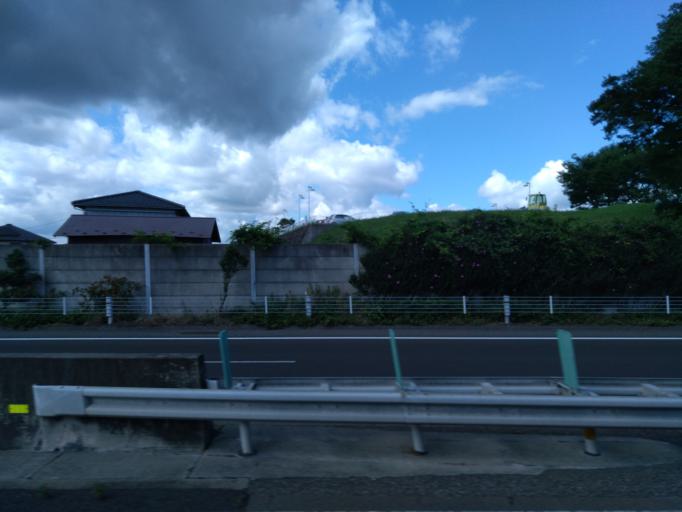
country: JP
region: Miyagi
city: Tomiya
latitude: 38.3340
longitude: 140.8558
